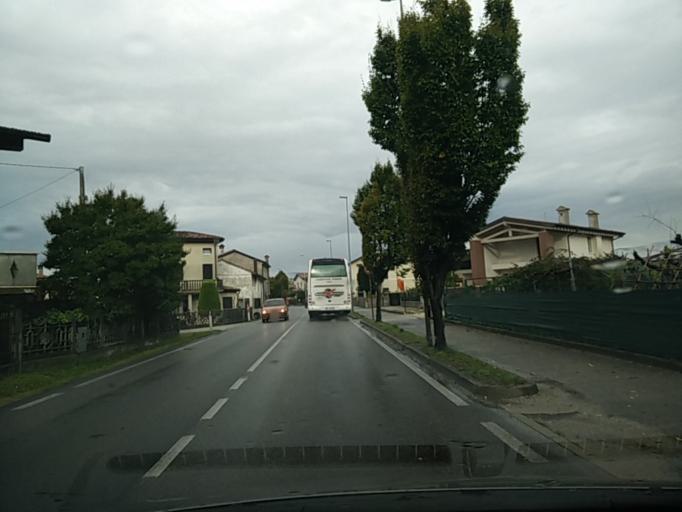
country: IT
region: Veneto
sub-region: Provincia di Vicenza
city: Rossano Veneto
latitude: 45.7030
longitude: 11.8165
